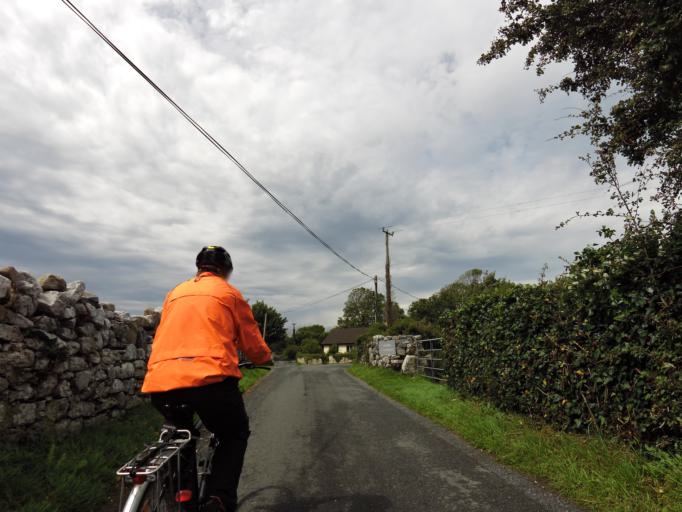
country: IE
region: Connaught
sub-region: County Galway
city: Gaillimh
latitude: 53.3007
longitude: -9.0724
